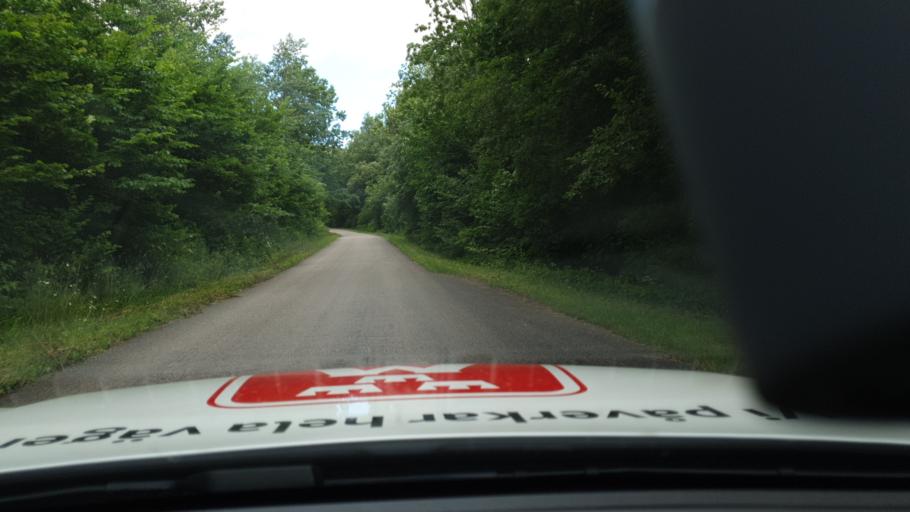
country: SE
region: Vaestra Goetaland
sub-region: Falkopings Kommun
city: Falkoeping
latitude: 58.1310
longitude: 13.6117
